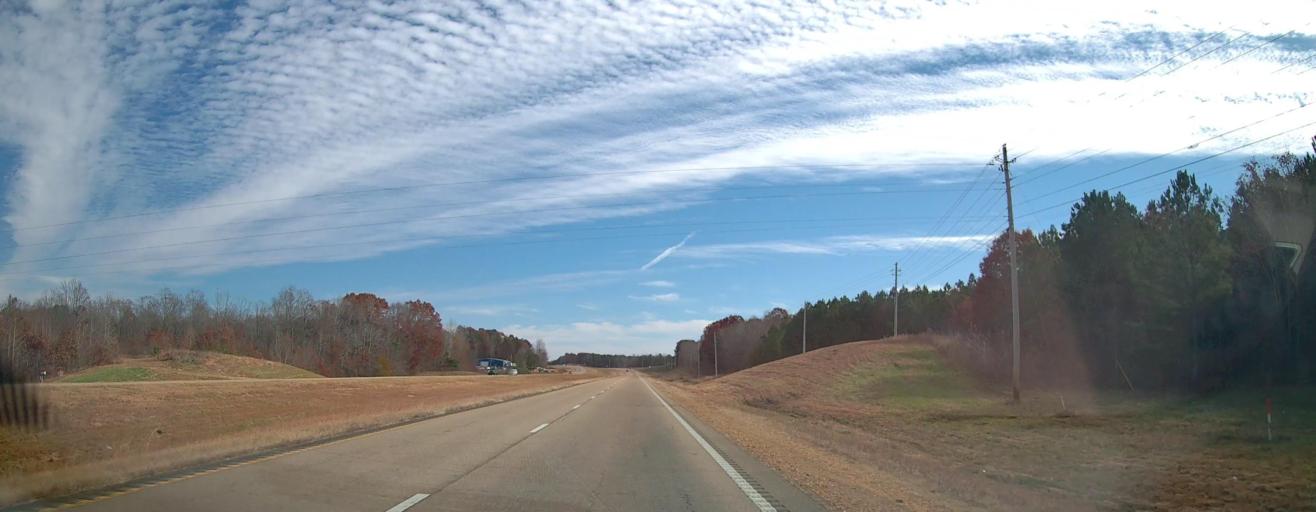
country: US
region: Mississippi
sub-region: Alcorn County
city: Corinth
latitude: 34.9342
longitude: -88.7245
